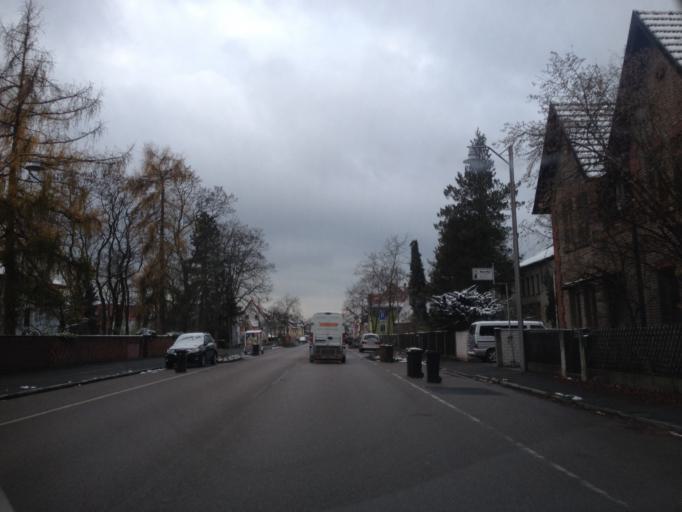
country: DE
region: Bavaria
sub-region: Regierungsbezirk Mittelfranken
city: Schwaig
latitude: 49.4828
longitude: 11.2040
